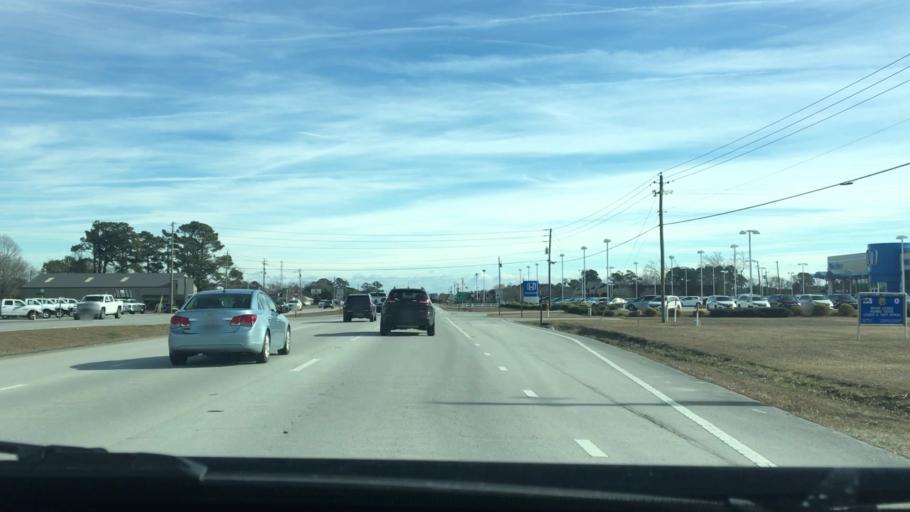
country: US
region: North Carolina
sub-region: Carteret County
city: Pine Knoll Shores
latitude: 34.7424
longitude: -76.8214
